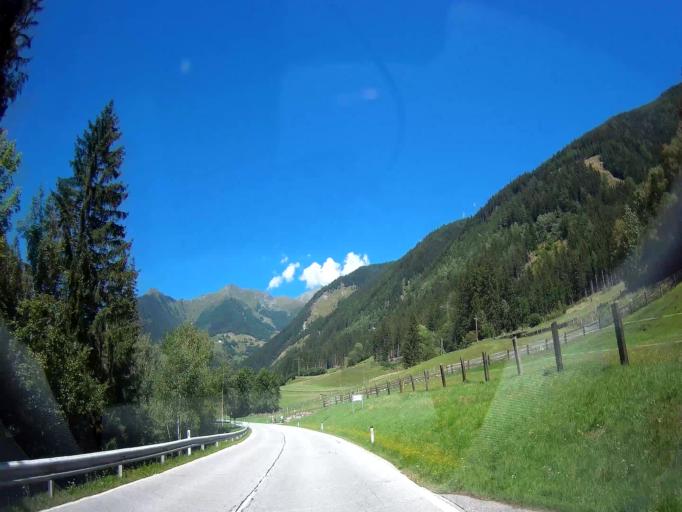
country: AT
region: Carinthia
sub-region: Politischer Bezirk Spittal an der Drau
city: Obervellach
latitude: 46.9549
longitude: 13.1846
